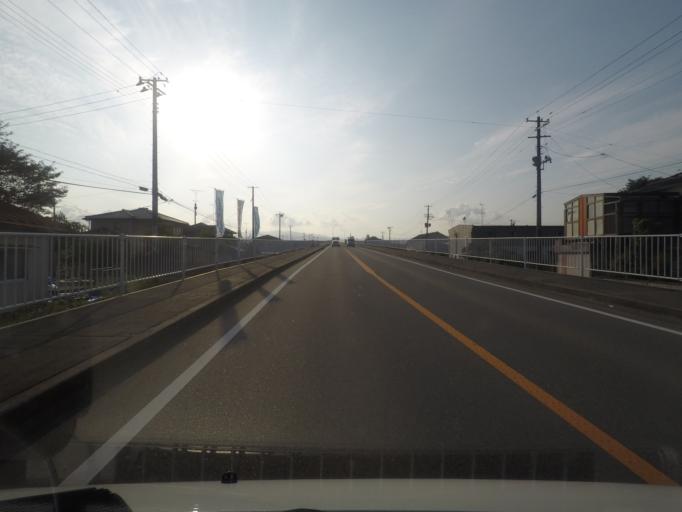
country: JP
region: Fukushima
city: Namie
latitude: 37.4957
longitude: 140.9866
